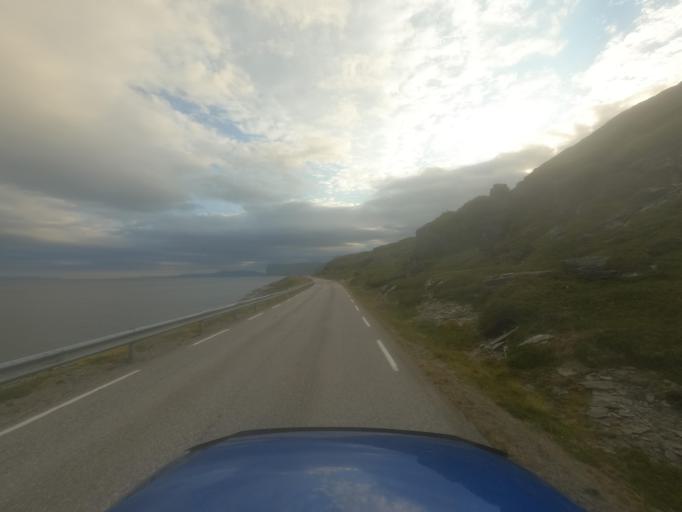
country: NO
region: Finnmark Fylke
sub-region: Nordkapp
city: Honningsvag
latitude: 70.6769
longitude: 25.4688
